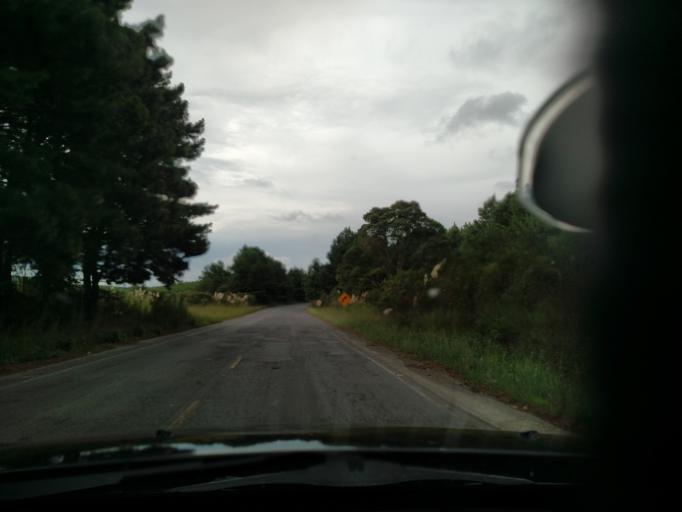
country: BR
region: Santa Catarina
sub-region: Otacilio Costa
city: Otacilio Costa
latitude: -27.6249
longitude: -50.1905
